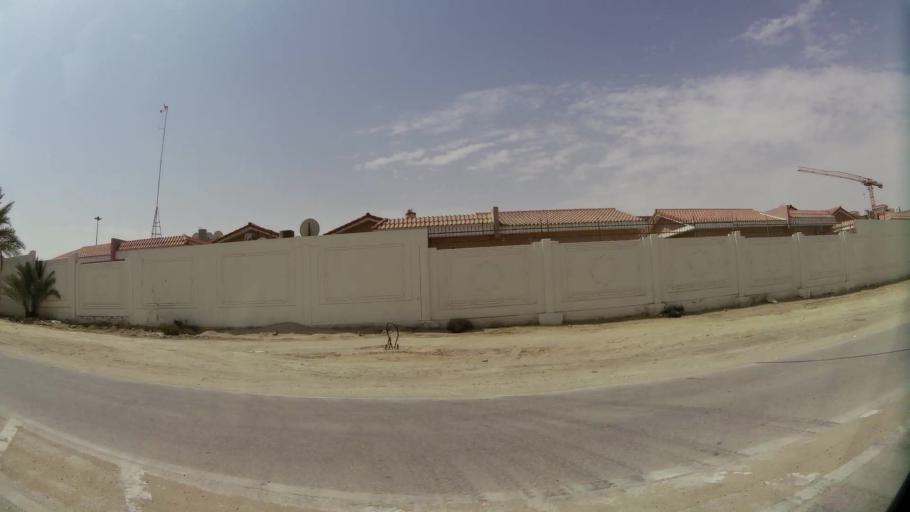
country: QA
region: Baladiyat ar Rayyan
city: Ar Rayyan
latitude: 25.3491
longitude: 51.4703
